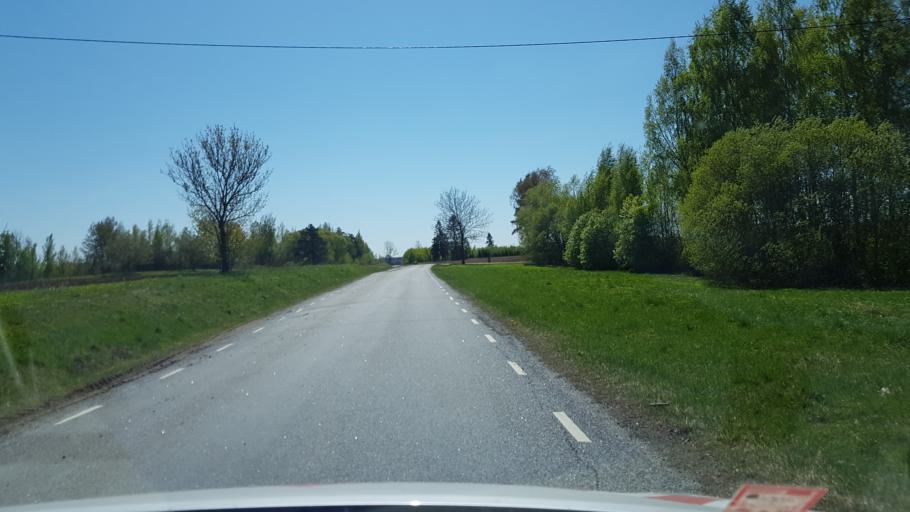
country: EE
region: Vorumaa
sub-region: Voru linn
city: Voru
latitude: 57.9281
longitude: 26.9513
